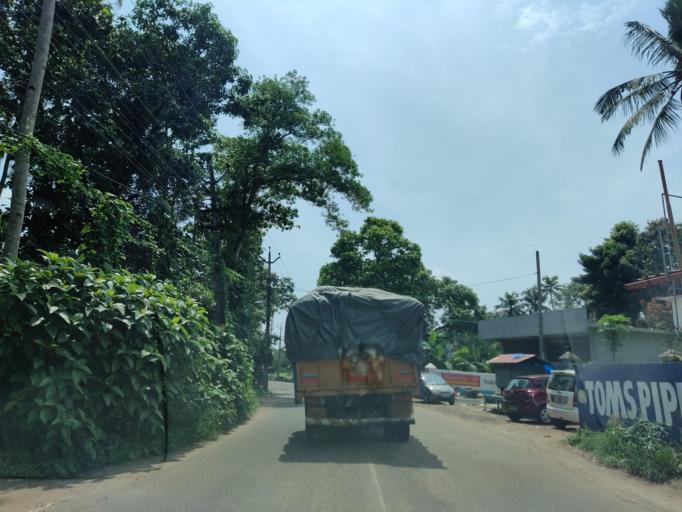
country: IN
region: Kerala
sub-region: Alappuzha
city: Chengannur
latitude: 9.3081
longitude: 76.5793
